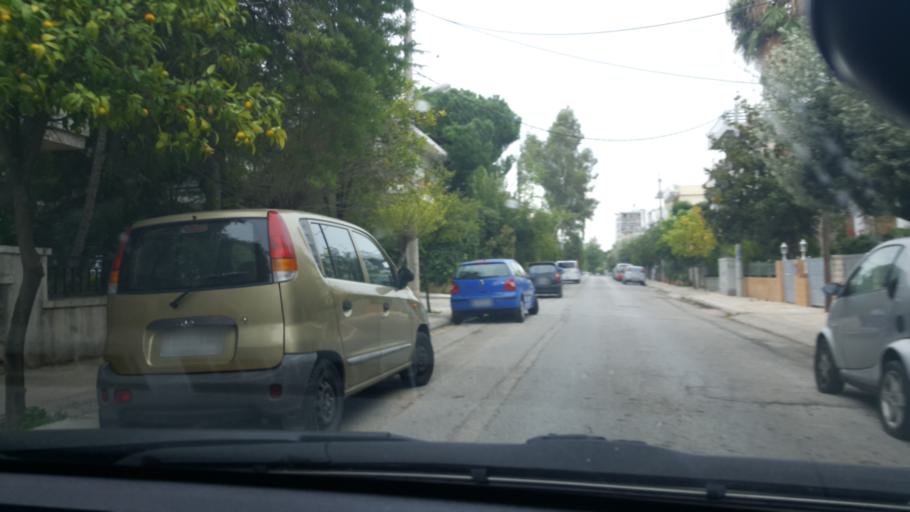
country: GR
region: Attica
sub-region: Nomarchia Athinas
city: Neo Psychiko
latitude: 38.0134
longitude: 23.7852
